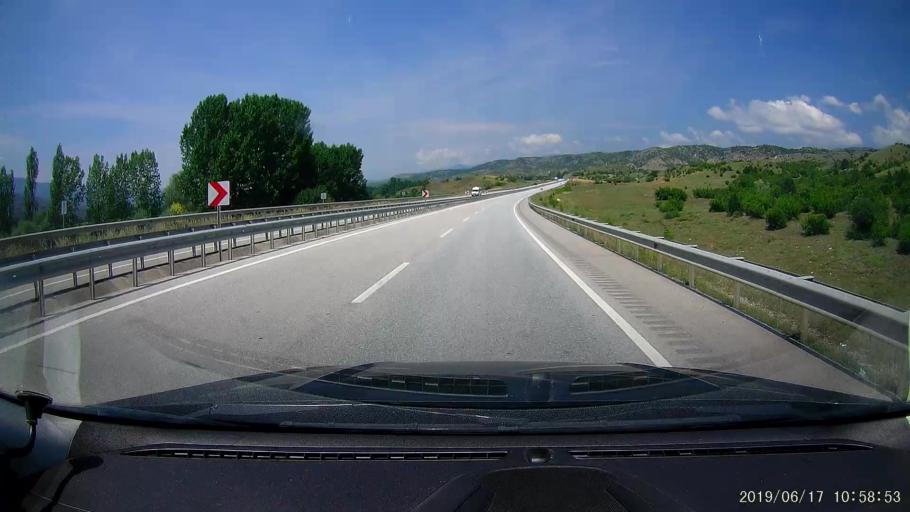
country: TR
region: Kastamonu
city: Tosya
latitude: 41.0401
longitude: 34.2143
